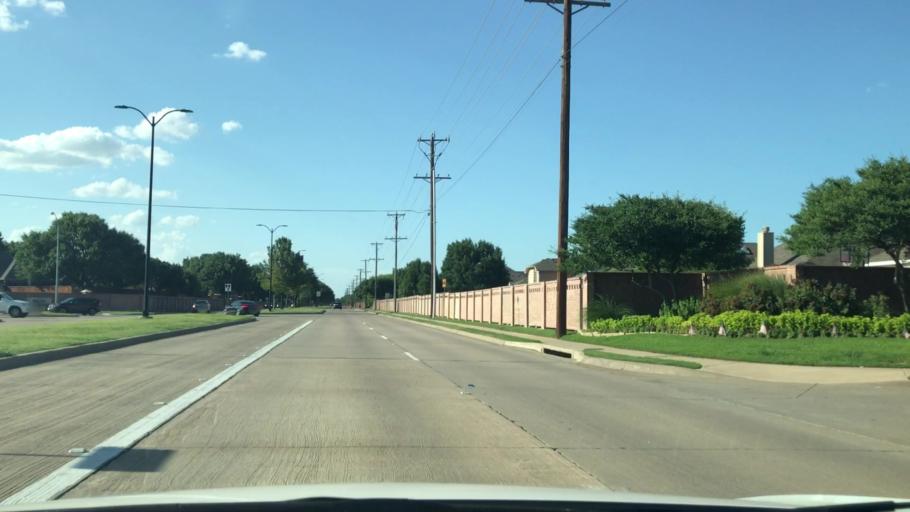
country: US
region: Texas
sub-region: Collin County
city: Frisco
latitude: 33.1083
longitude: -96.7881
